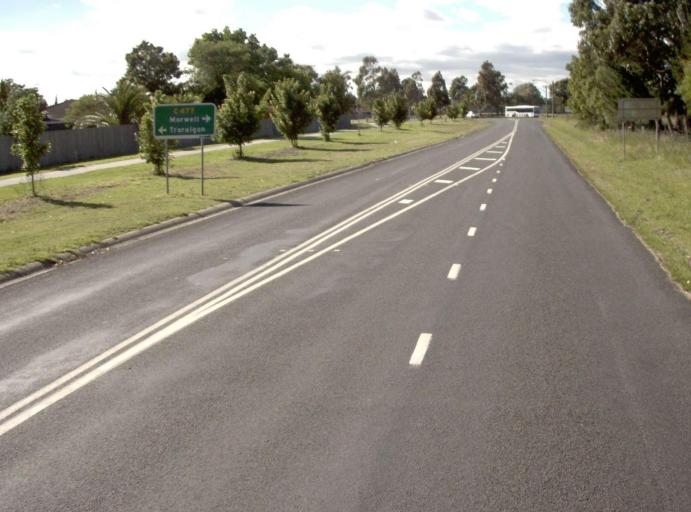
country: AU
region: Victoria
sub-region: Latrobe
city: Traralgon
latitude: -38.1886
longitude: 146.5045
